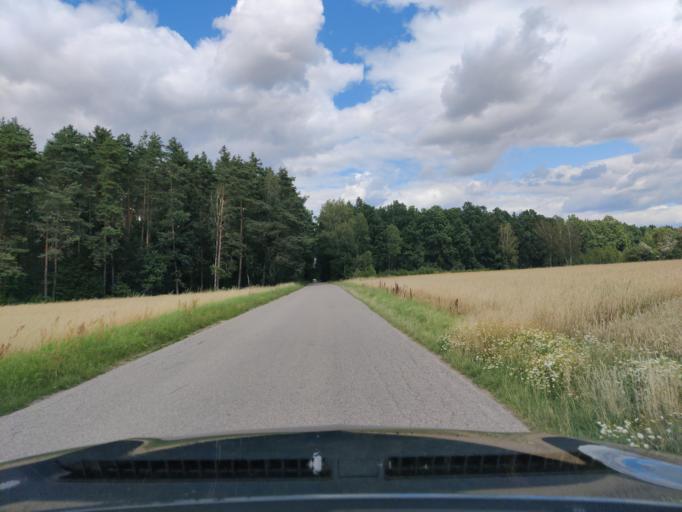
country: PL
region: Masovian Voivodeship
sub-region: Powiat wegrowski
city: Miedzna
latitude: 52.4907
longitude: 22.0285
